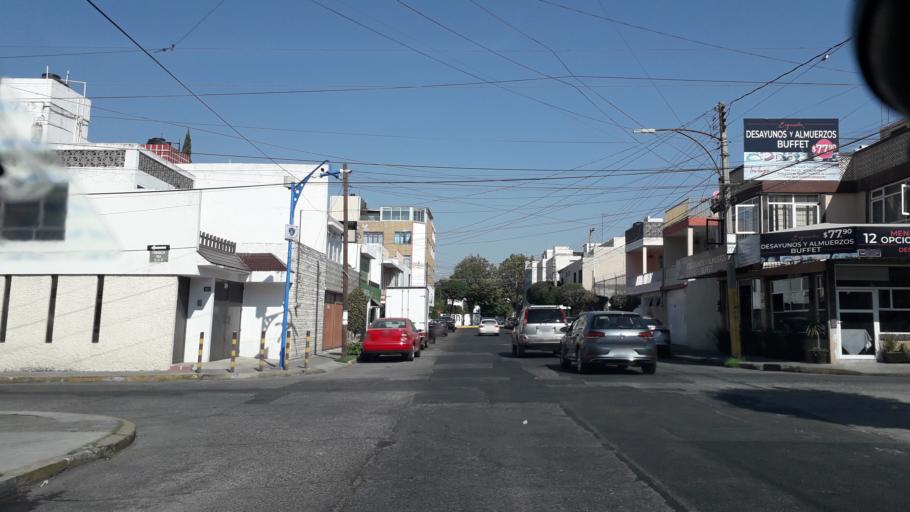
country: MX
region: Puebla
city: Puebla
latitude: 19.0313
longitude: -98.2147
